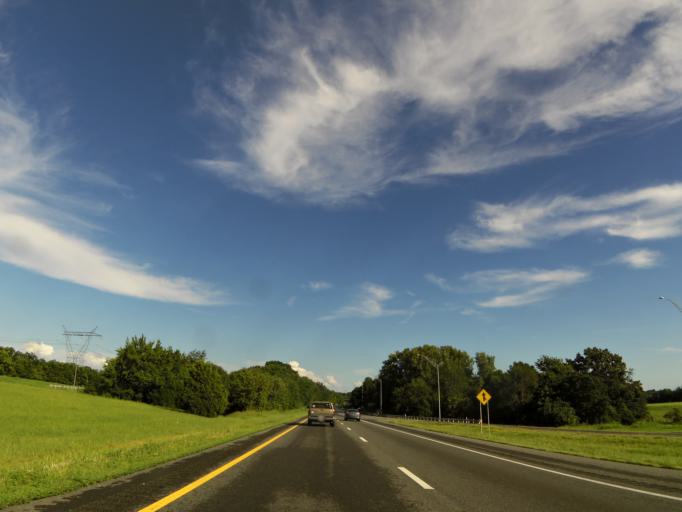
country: US
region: Kentucky
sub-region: Todd County
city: Guthrie
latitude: 36.5237
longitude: -87.2197
